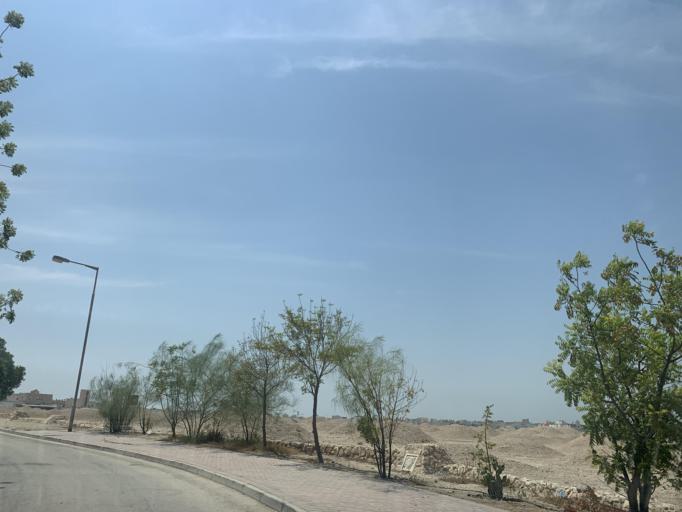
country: BH
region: Central Governorate
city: Madinat Hamad
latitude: 26.1402
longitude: 50.5061
